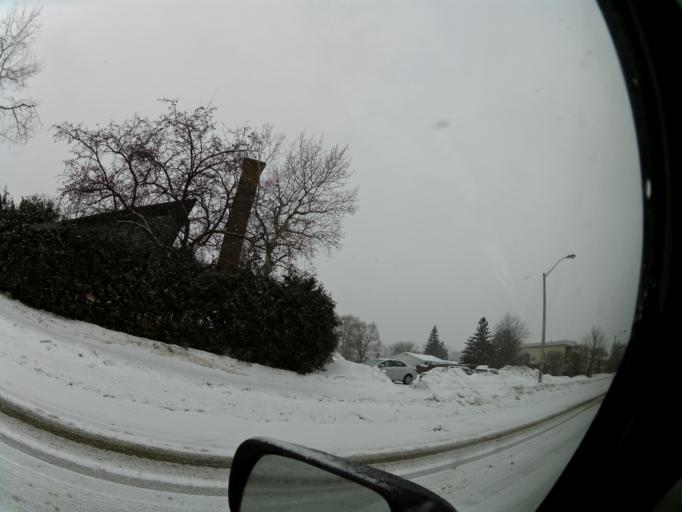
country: CA
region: Ontario
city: Ottawa
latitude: 45.4060
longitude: -75.6503
